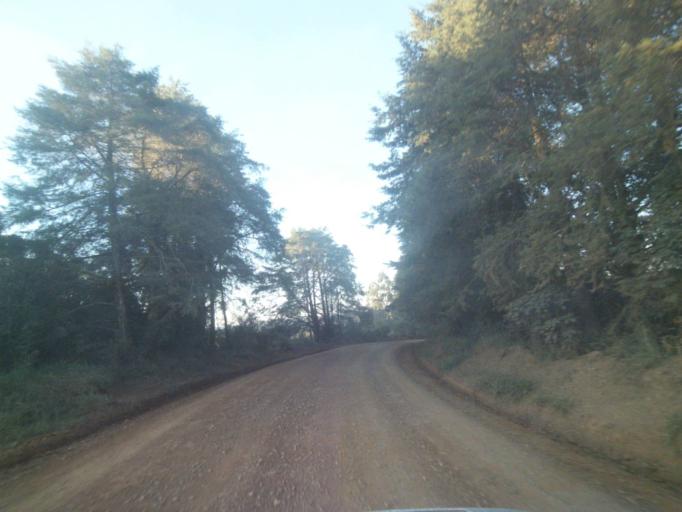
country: BR
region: Parana
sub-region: Tibagi
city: Tibagi
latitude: -24.5268
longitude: -50.5099
